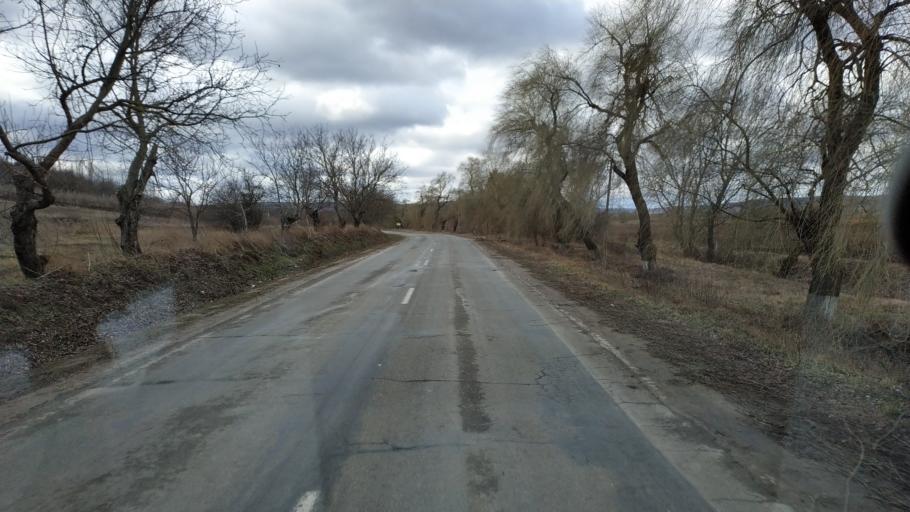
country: MD
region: Stinga Nistrului
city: Bucovat
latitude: 47.1491
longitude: 28.4035
